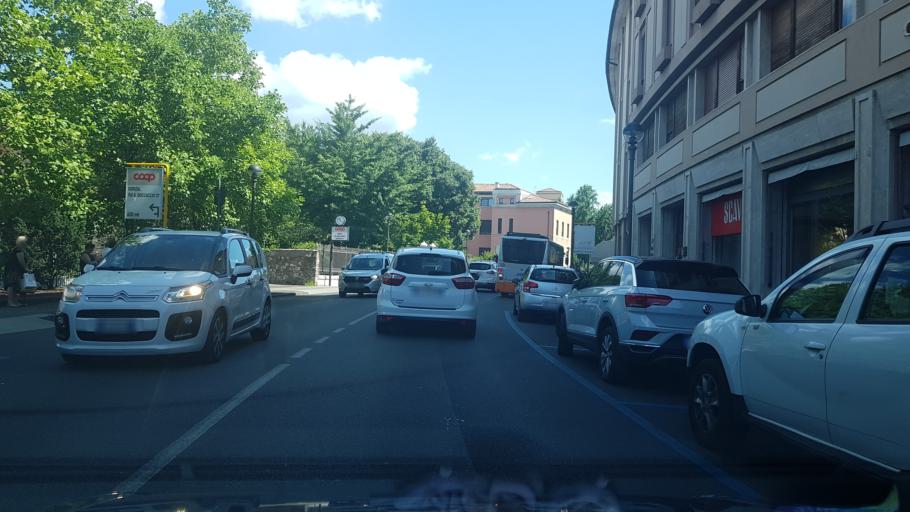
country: IT
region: Friuli Venezia Giulia
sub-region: Provincia di Gorizia
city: Gorizia
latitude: 45.9421
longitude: 13.6219
